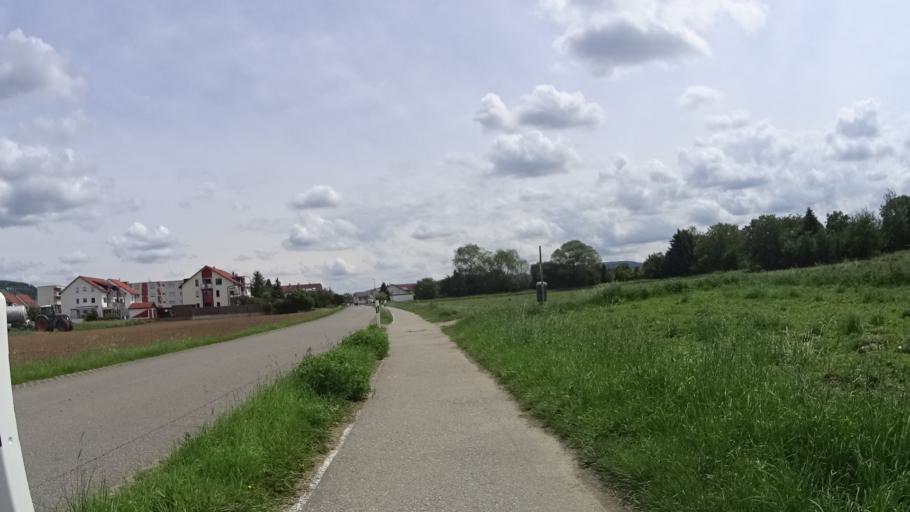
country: DE
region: Baden-Wuerttemberg
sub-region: Freiburg Region
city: Grenzach-Wyhlen
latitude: 47.5455
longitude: 7.6802
